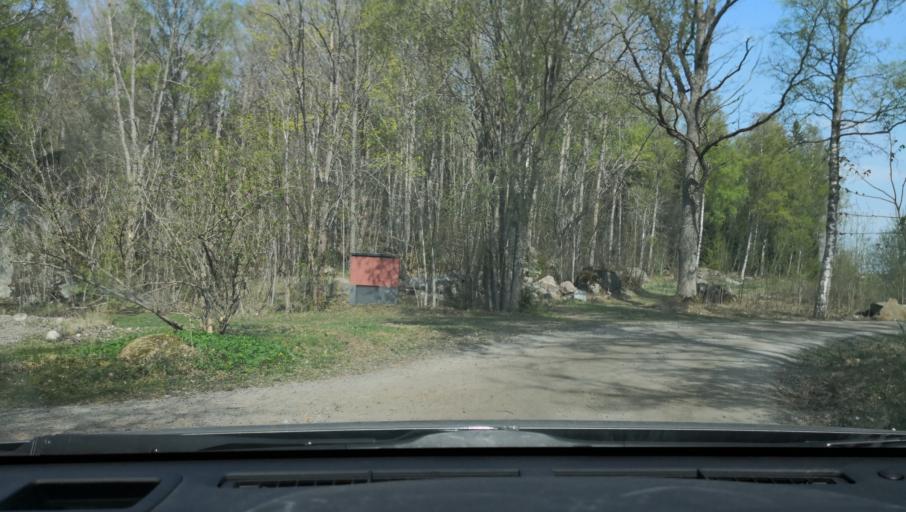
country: SE
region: Vaestmanland
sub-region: Vasteras
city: Skultuna
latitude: 59.7627
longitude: 16.4533
